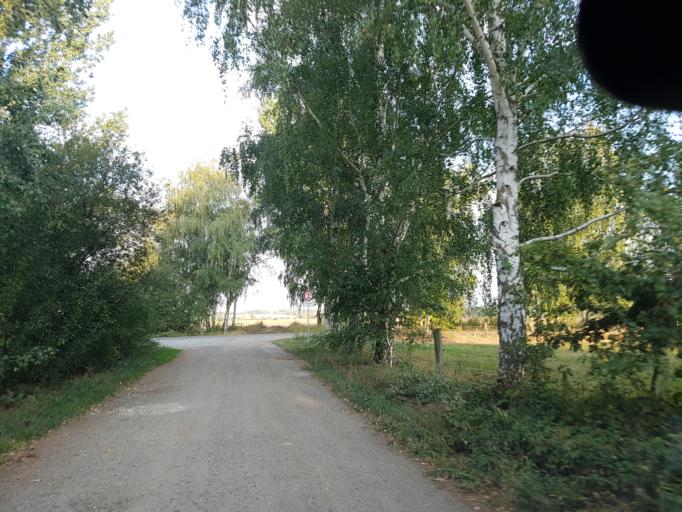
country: DE
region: Brandenburg
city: Hohenleipisch
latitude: 51.4611
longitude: 13.5613
